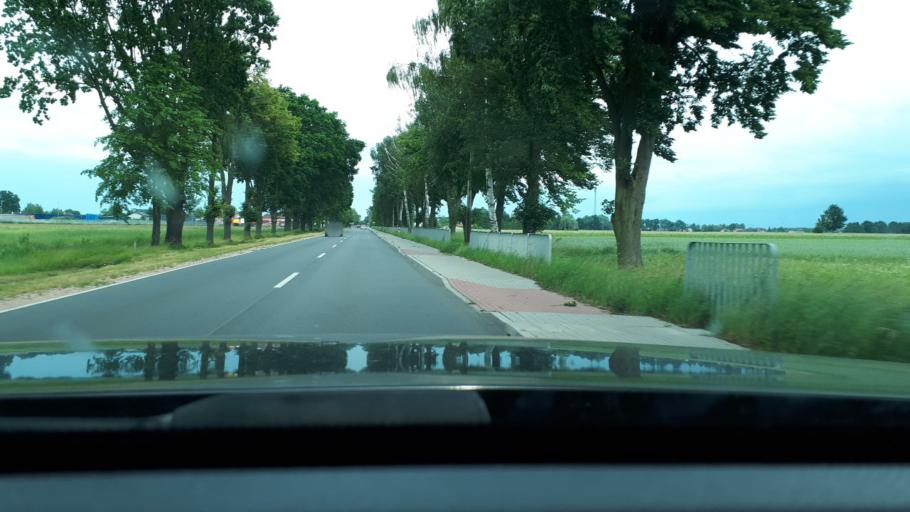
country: PL
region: Masovian Voivodeship
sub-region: Powiat warszawski zachodni
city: Kampinos
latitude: 52.2691
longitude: 20.4472
